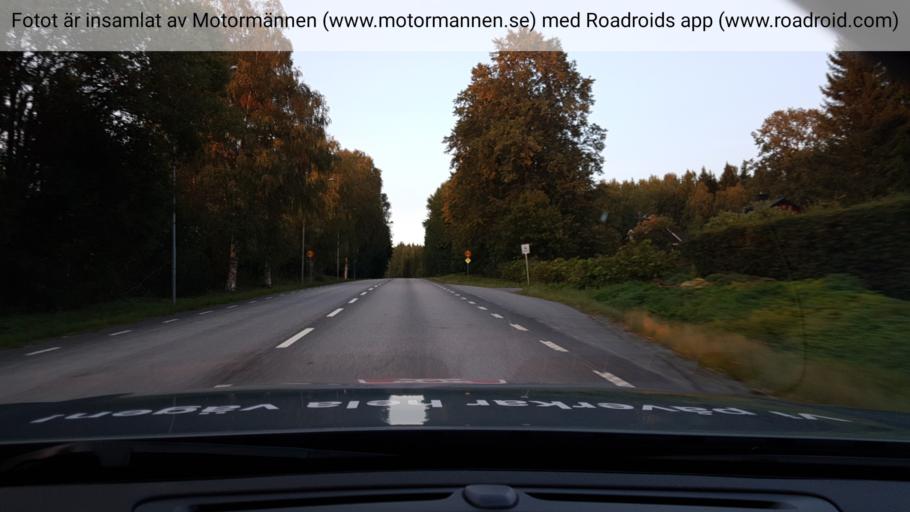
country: SE
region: OErebro
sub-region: Hallefors Kommun
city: Haellefors
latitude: 59.7885
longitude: 14.5368
